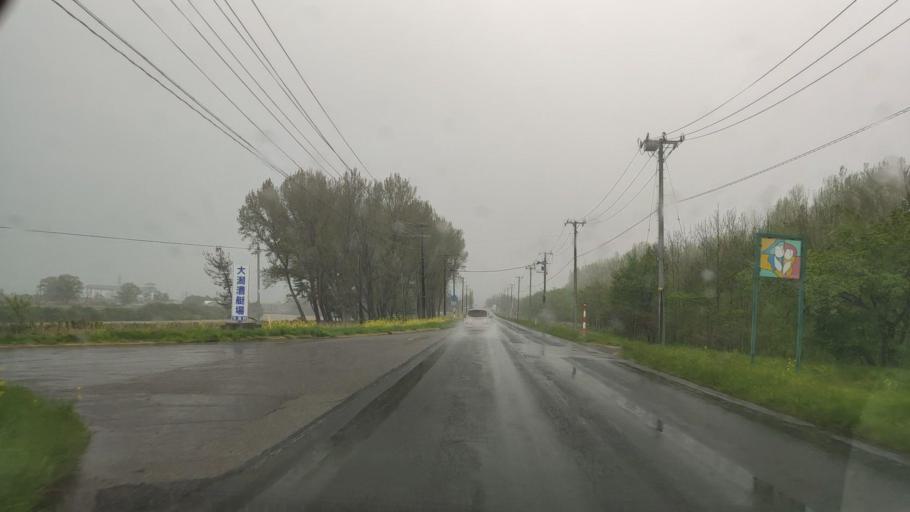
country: JP
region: Akita
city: Tenno
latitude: 39.9493
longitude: 139.9458
